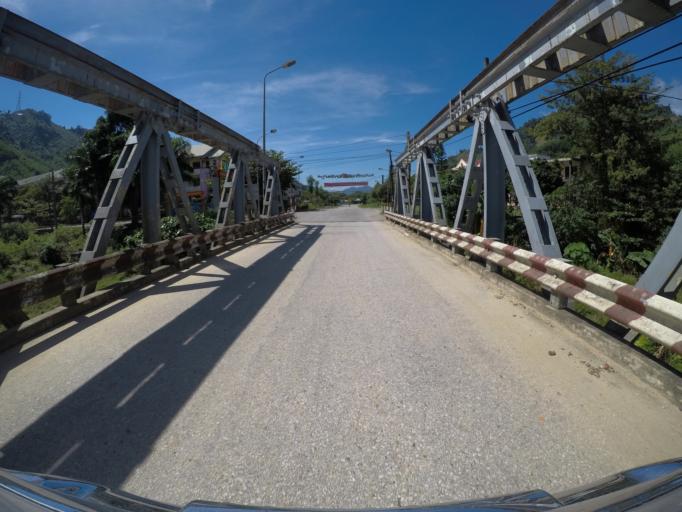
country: VN
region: Quang Nam
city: Thanh My
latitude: 15.6910
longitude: 107.7666
